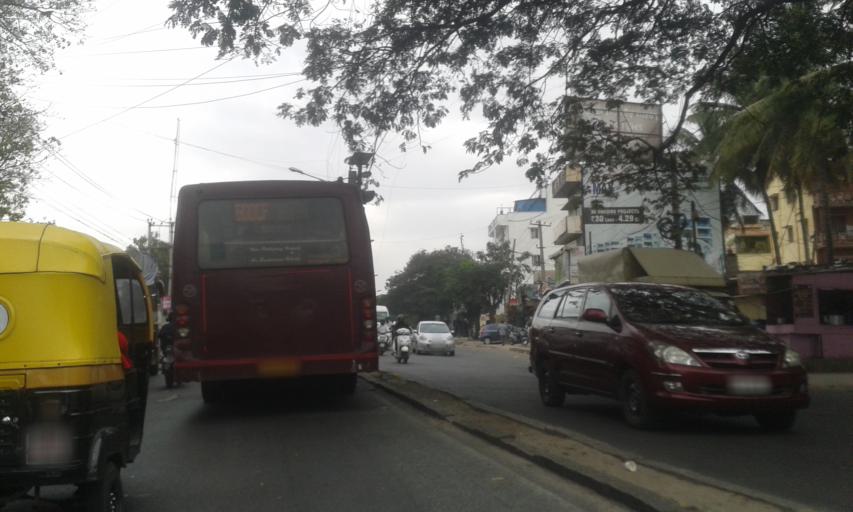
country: IN
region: Karnataka
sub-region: Bangalore Urban
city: Bangalore
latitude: 12.9162
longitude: 77.6172
